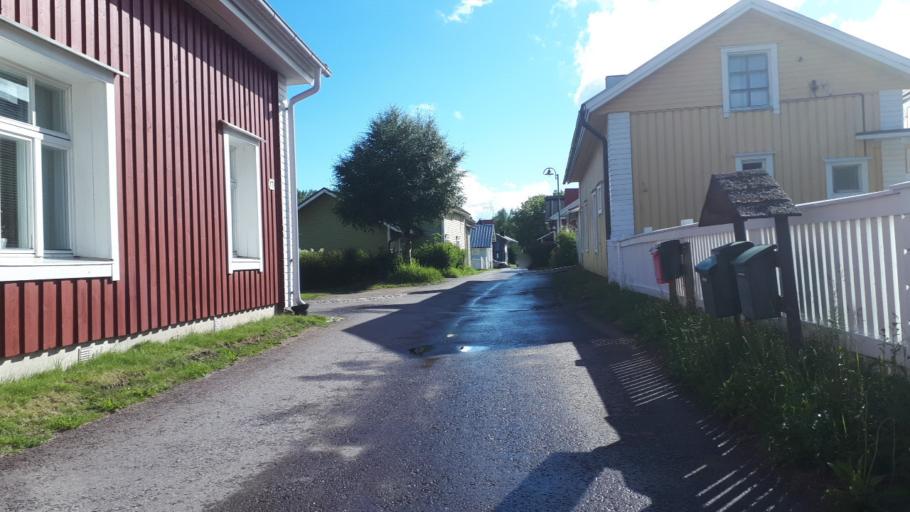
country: FI
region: Northern Ostrobothnia
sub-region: Oulunkaari
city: Ii
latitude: 65.3256
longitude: 25.3714
